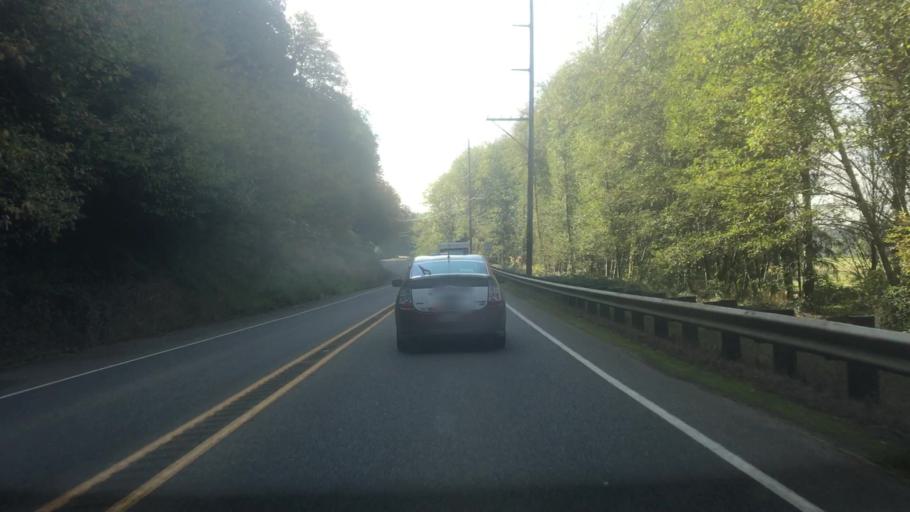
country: US
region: Washington
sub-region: Grays Harbor County
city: Montesano
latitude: 46.9574
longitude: -123.6063
